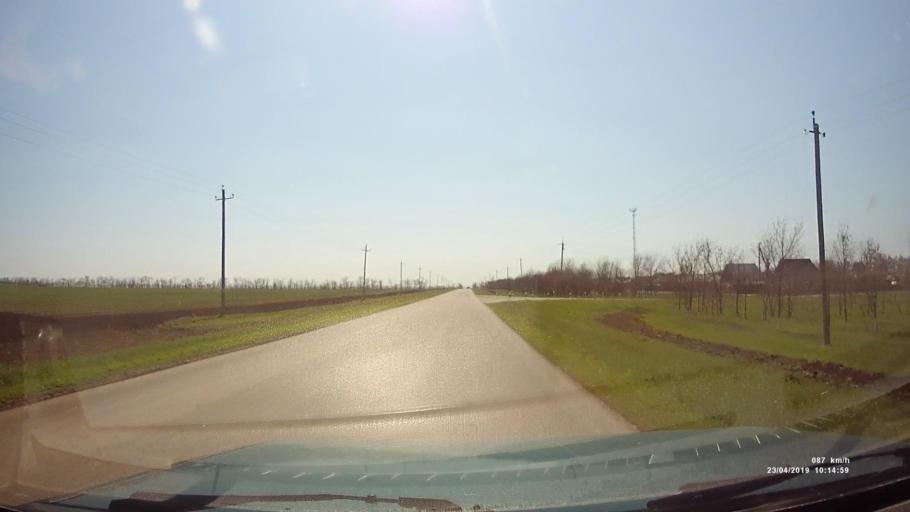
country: RU
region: Rostov
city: Sovetskoye
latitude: 46.6716
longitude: 42.3762
